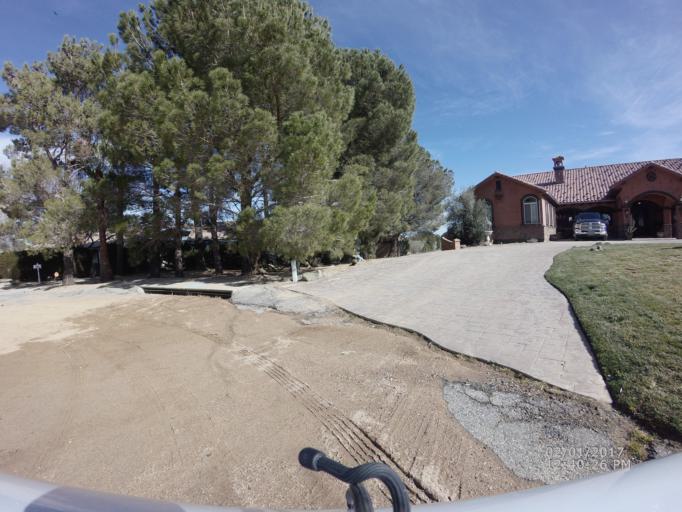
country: US
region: California
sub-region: Los Angeles County
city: Desert View Highlands
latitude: 34.5565
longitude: -118.1478
